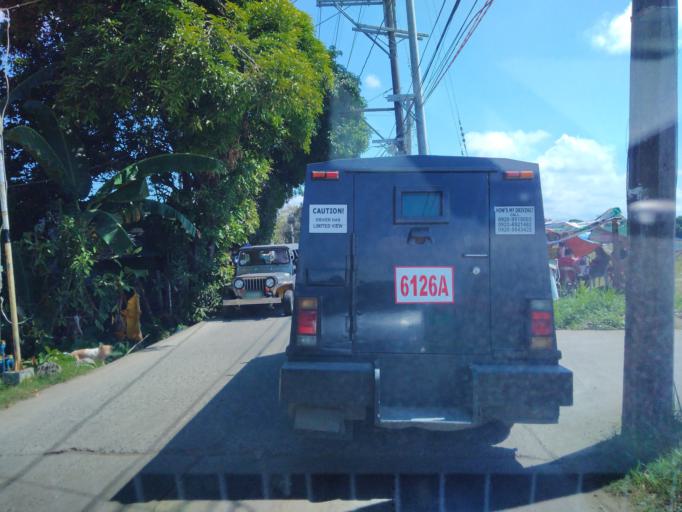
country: PH
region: Central Luzon
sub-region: Province of Bulacan
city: Balasing
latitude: 14.8580
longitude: 121.0199
